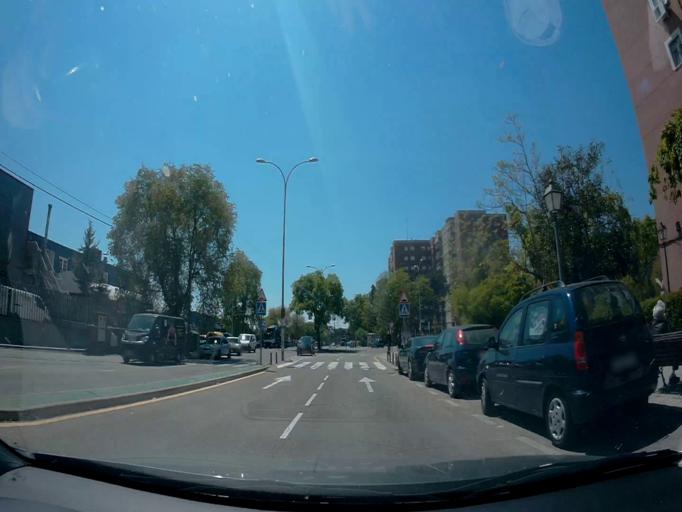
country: ES
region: Madrid
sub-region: Provincia de Madrid
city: Alcorcon
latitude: 40.3498
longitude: -3.8025
